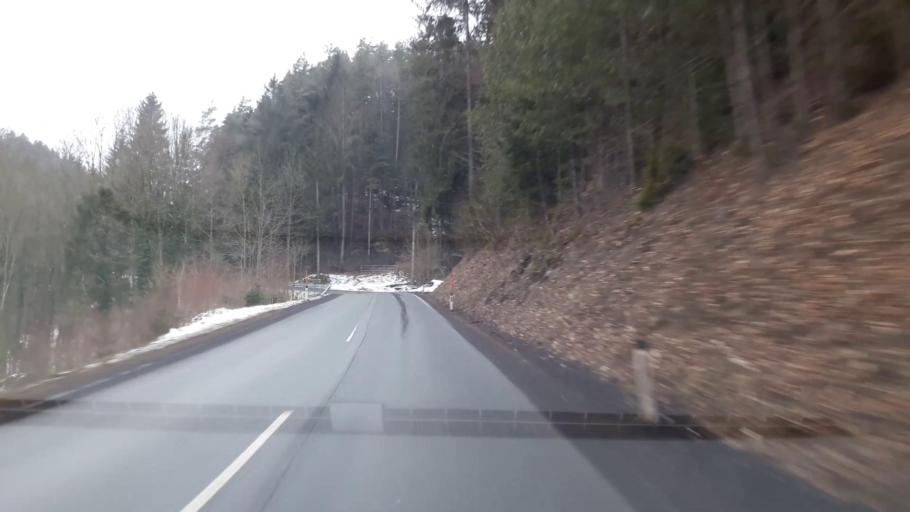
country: AT
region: Lower Austria
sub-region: Politischer Bezirk Neunkirchen
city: Feistritz am Wechsel
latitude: 47.5559
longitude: 16.0724
